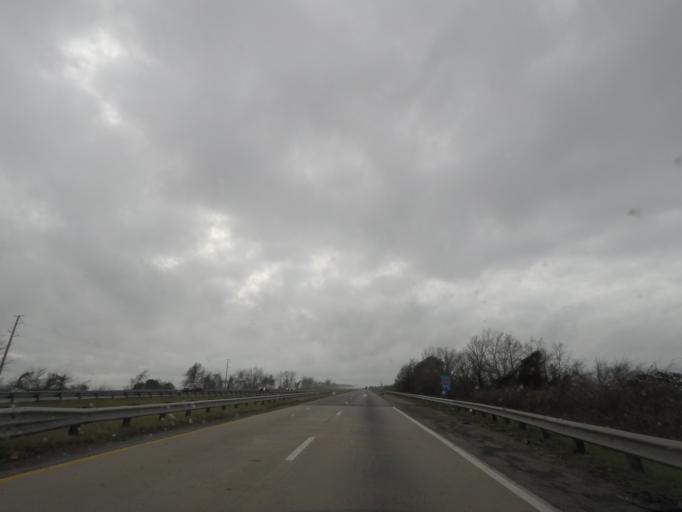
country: US
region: South Carolina
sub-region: Orangeburg County
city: Holly Hill
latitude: 33.5180
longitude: -80.4362
